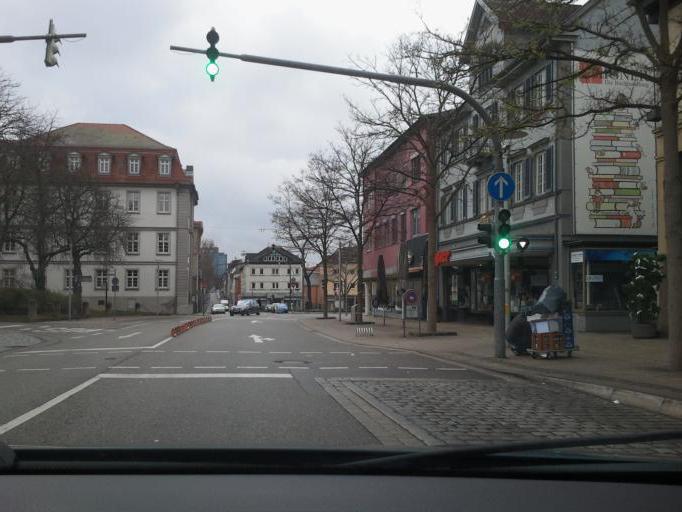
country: DE
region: Baden-Wuerttemberg
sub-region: Regierungsbezirk Stuttgart
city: Ludwigsburg
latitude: 48.8956
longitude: 9.1882
